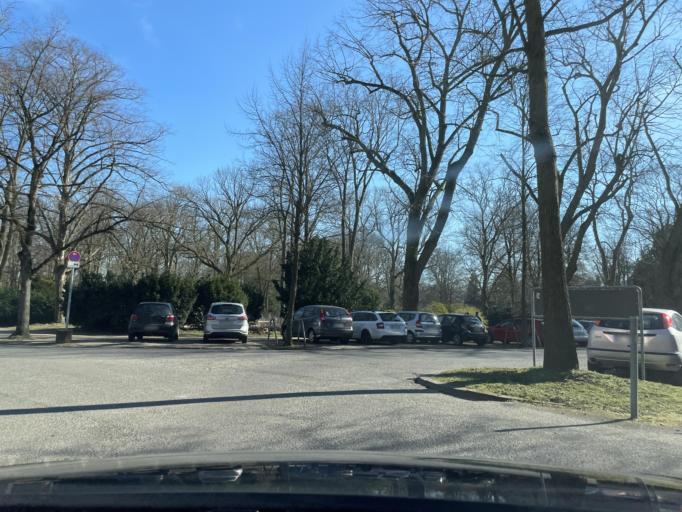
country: DE
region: North Rhine-Westphalia
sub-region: Regierungsbezirk Dusseldorf
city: Monchengladbach
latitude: 51.2038
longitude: 6.4309
